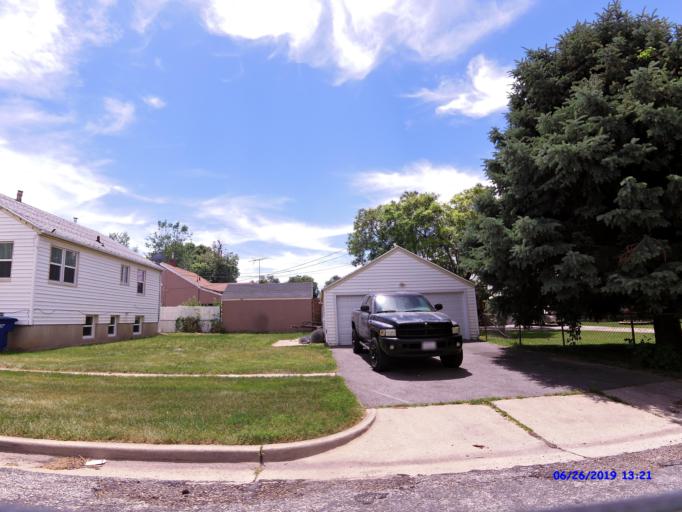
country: US
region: Utah
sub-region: Weber County
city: South Ogden
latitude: 41.2069
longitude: -111.9601
